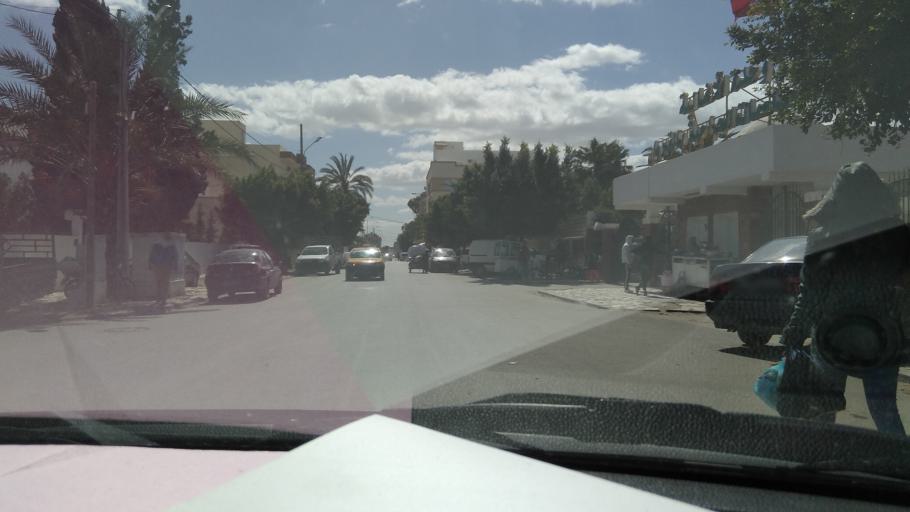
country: TN
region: Al Qayrawan
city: Kairouan
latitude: 35.6687
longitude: 10.1077
